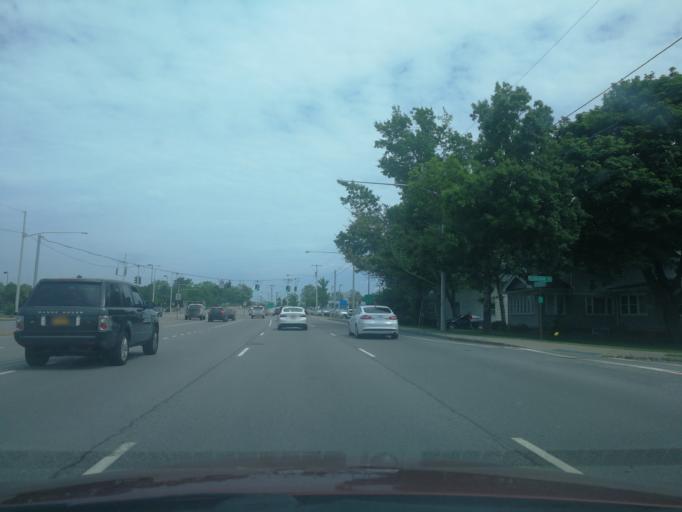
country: US
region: New York
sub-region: Monroe County
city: Greece
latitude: 43.2047
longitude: -77.6637
